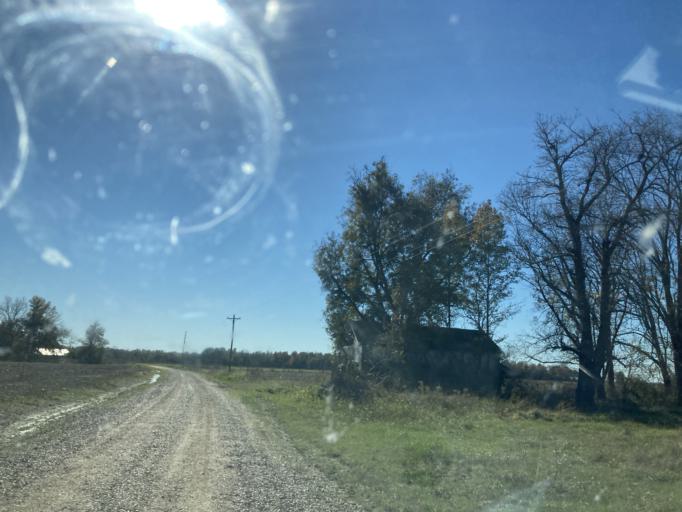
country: US
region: Mississippi
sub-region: Hinds County
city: Lynchburg
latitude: 32.6383
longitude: -90.6130
